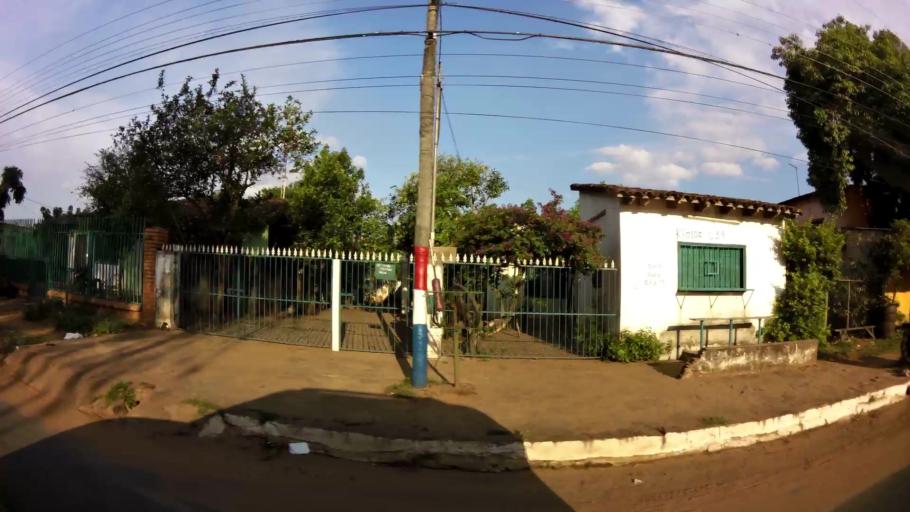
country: PY
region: Central
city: Nemby
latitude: -25.3666
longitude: -57.5308
